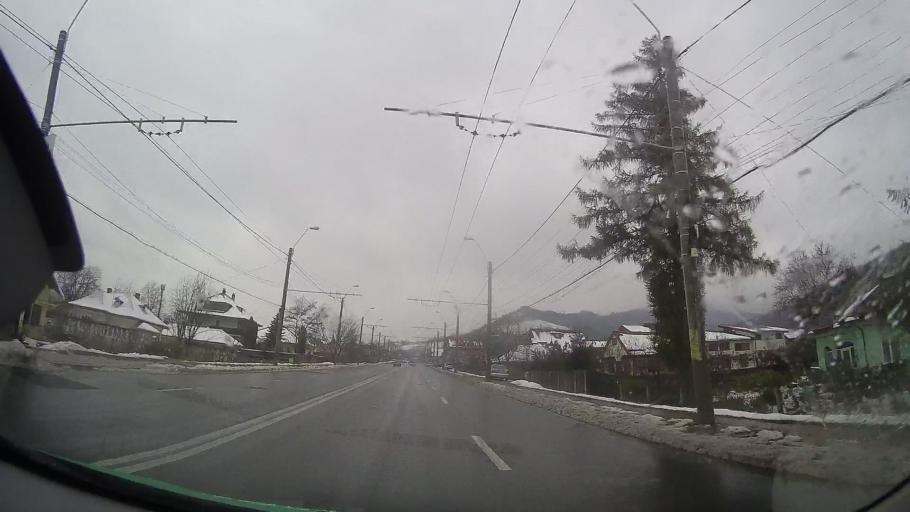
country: RO
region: Neamt
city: Piatra Neamt
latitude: 46.9394
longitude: 26.3348
